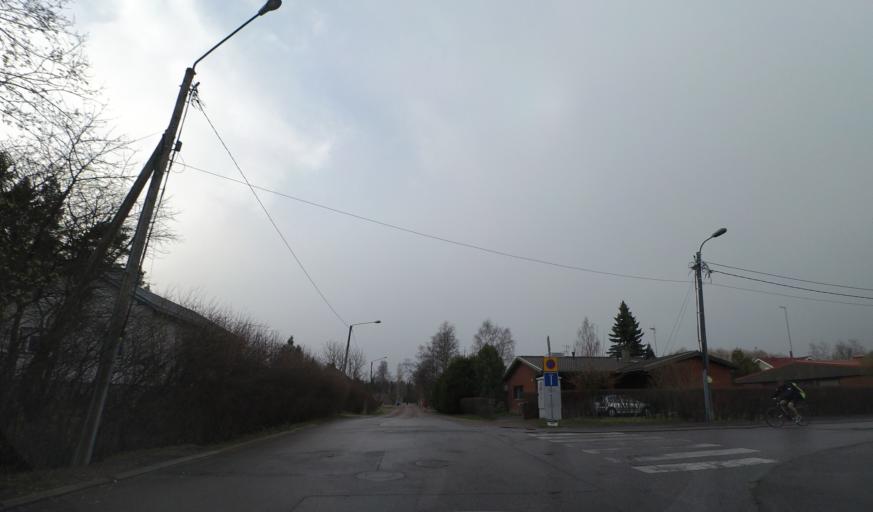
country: FI
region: Uusimaa
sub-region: Helsinki
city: Vantaa
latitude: 60.2705
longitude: 25.0177
